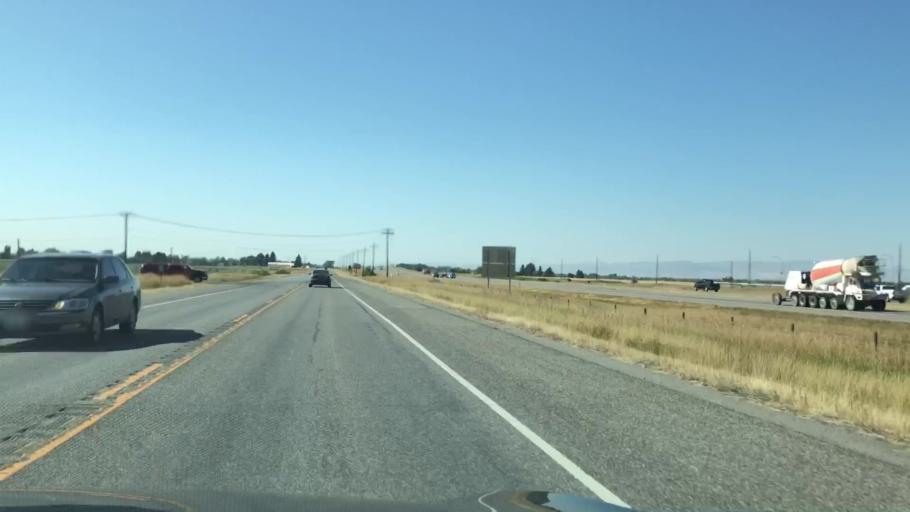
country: US
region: Montana
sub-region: Gallatin County
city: Bozeman
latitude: 45.7244
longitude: -111.0812
